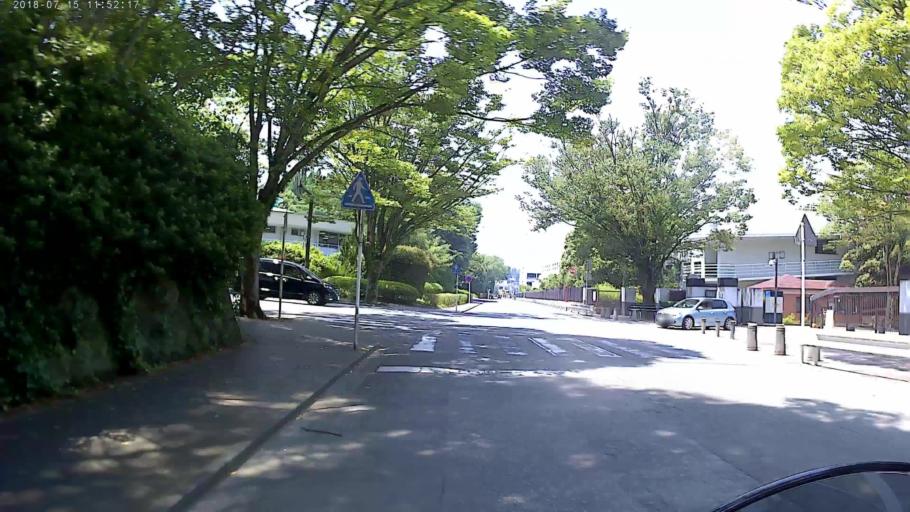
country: JP
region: Kanagawa
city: Isehara
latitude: 35.3605
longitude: 139.2735
